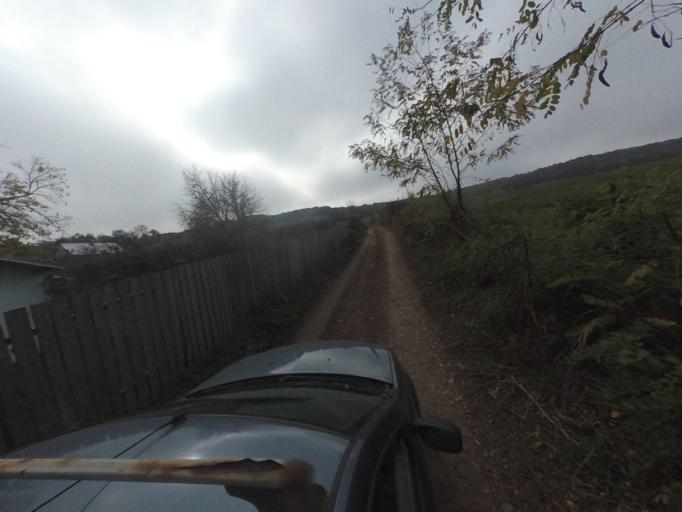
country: RO
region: Vaslui
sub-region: Comuna Bacesti
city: Bacesti
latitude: 46.8357
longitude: 27.2272
